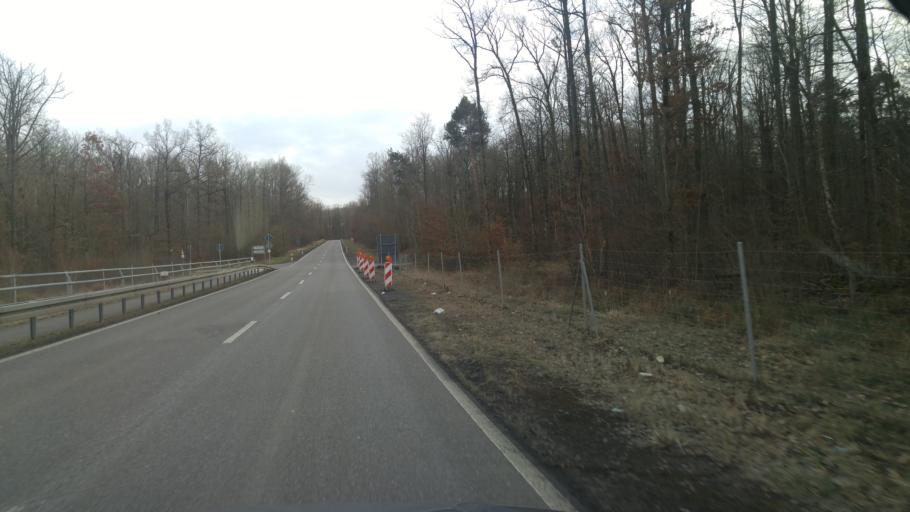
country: DE
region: Baden-Wuerttemberg
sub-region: Regierungsbezirk Stuttgart
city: Renningen
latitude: 48.7799
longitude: 8.9723
